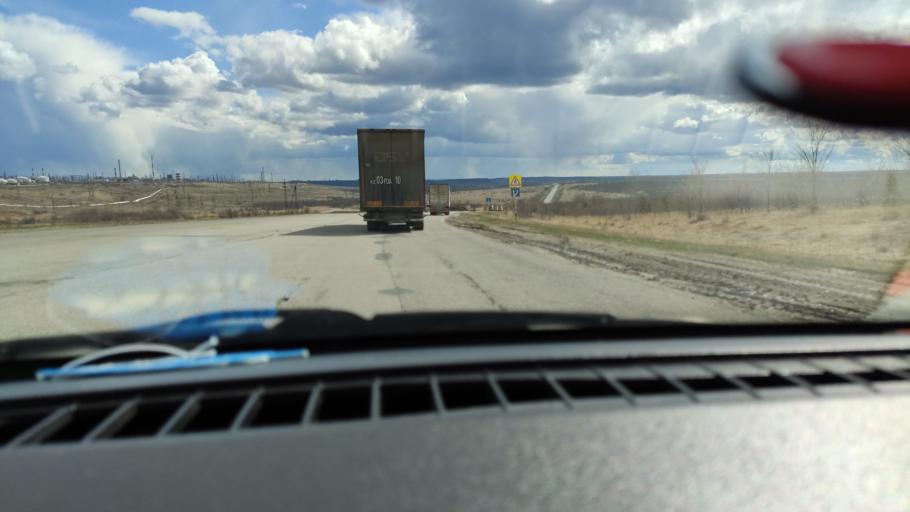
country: RU
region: Samara
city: Varlamovo
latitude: 53.1039
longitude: 48.3571
